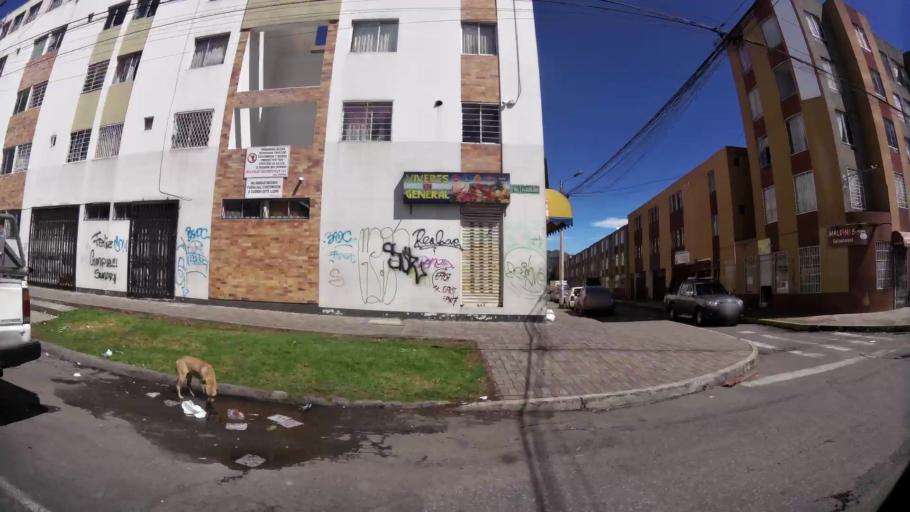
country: EC
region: Pichincha
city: Quito
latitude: -0.2978
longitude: -78.5471
